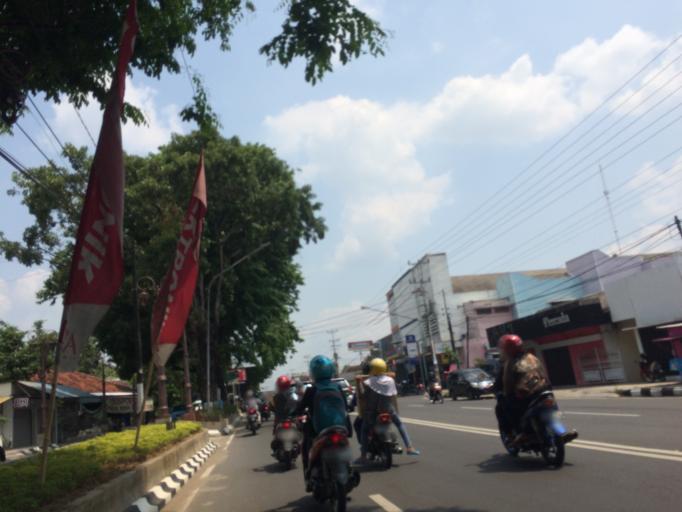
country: ID
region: Central Java
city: Grogol
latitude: -7.6722
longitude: 110.8390
